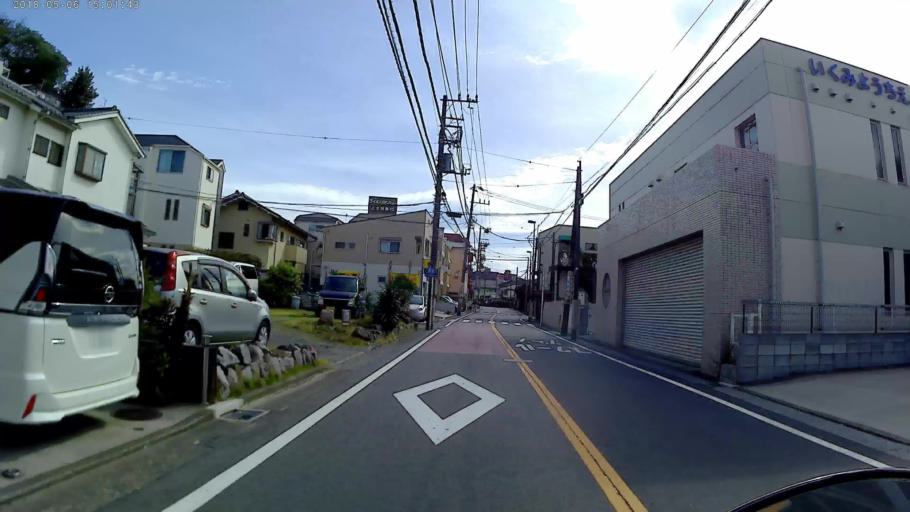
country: JP
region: Kanagawa
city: Yokohama
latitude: 35.4167
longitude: 139.6108
